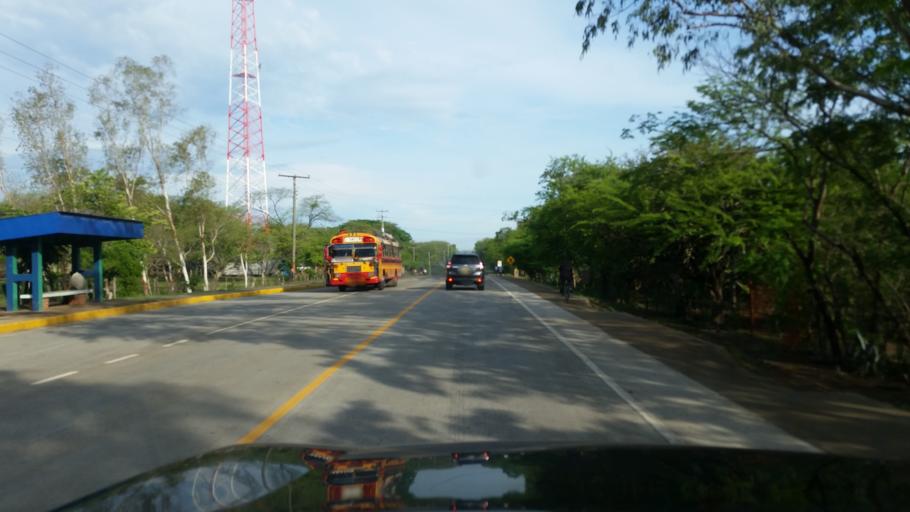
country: NI
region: Managua
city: Carlos Fonseca Amador
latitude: 12.0856
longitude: -86.5297
